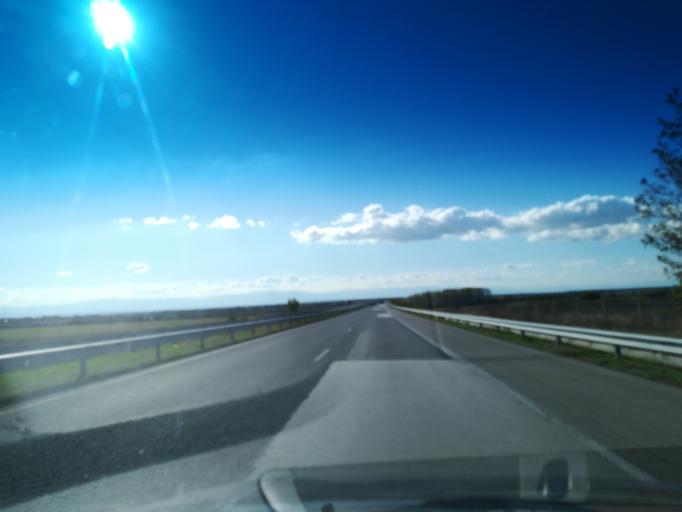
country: BG
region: Stara Zagora
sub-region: Obshtina Chirpan
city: Chirpan
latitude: 42.2216
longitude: 25.3364
